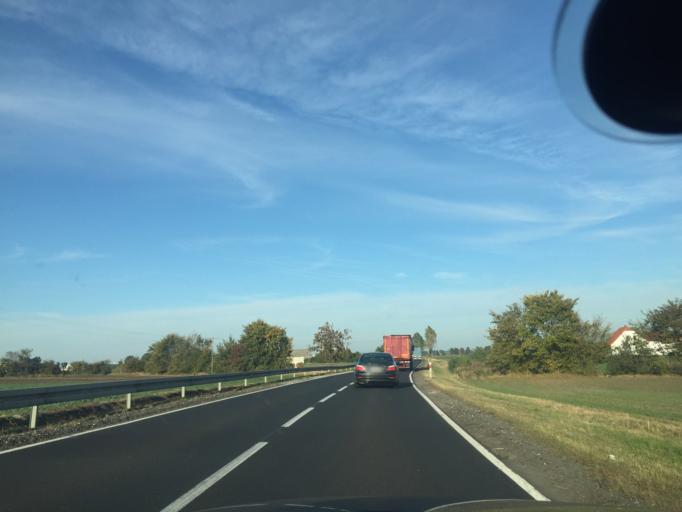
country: PL
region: Kujawsko-Pomorskie
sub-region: Powiat inowroclawski
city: Wierzchoslawice
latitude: 52.8583
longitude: 18.3513
